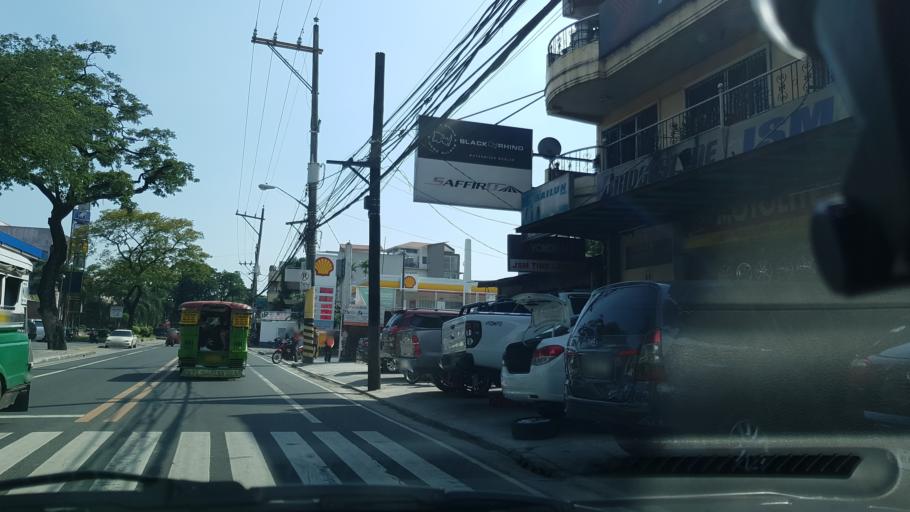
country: PH
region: Metro Manila
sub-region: Marikina
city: Calumpang
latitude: 14.6466
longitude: 121.0967
